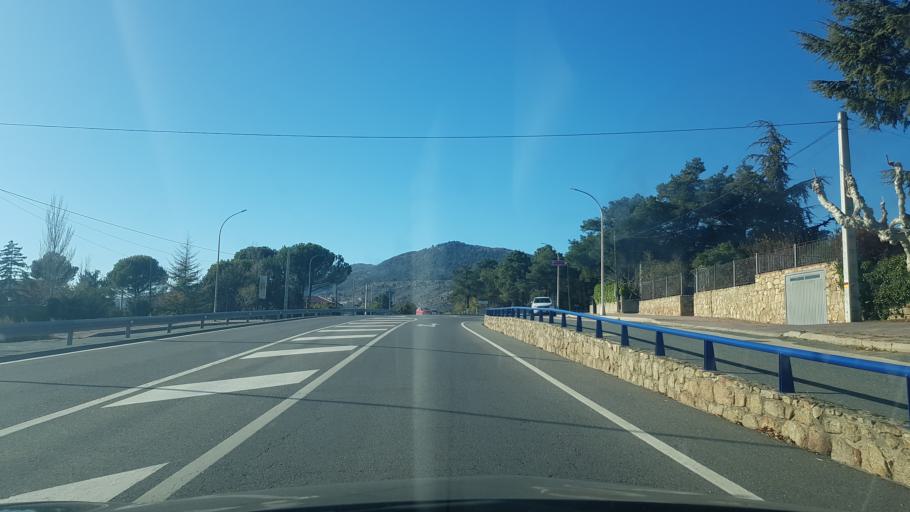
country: ES
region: Castille and Leon
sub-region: Provincia de Avila
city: Barraco
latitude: 40.4790
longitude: -4.6514
